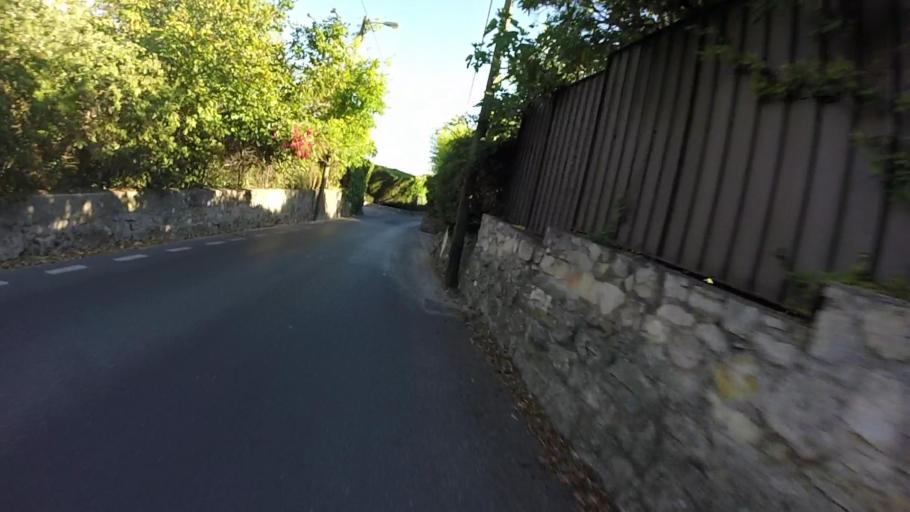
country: FR
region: Provence-Alpes-Cote d'Azur
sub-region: Departement des Alpes-Maritimes
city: Mougins
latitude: 43.6084
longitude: 7.0031
